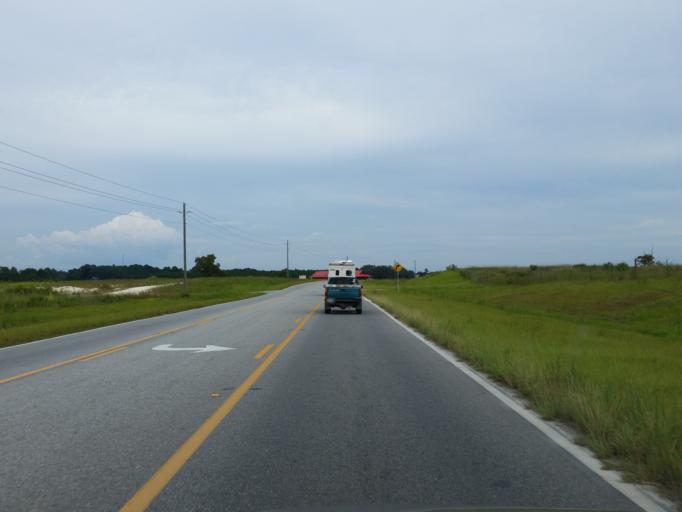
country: US
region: Florida
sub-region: Suwannee County
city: Live Oak
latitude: 30.3198
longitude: -82.9772
